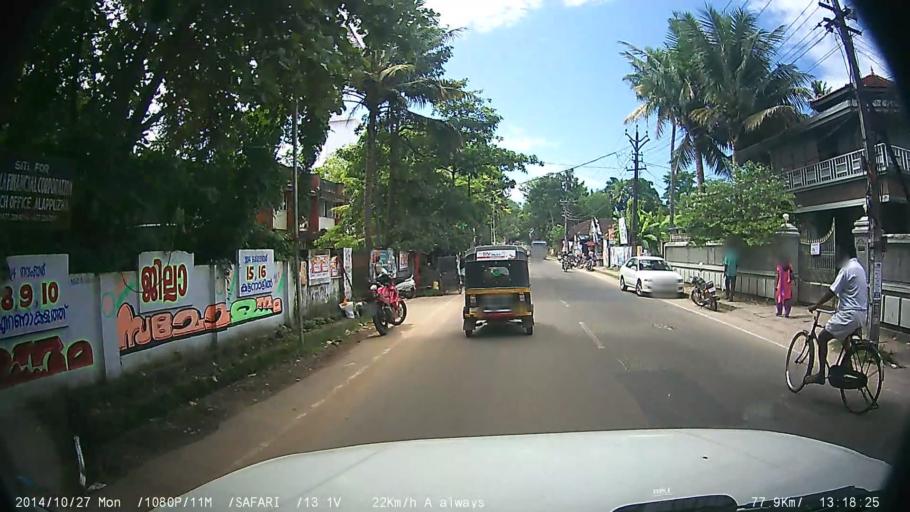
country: IN
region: Kerala
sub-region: Alappuzha
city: Alleppey
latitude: 9.4917
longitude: 76.3359
